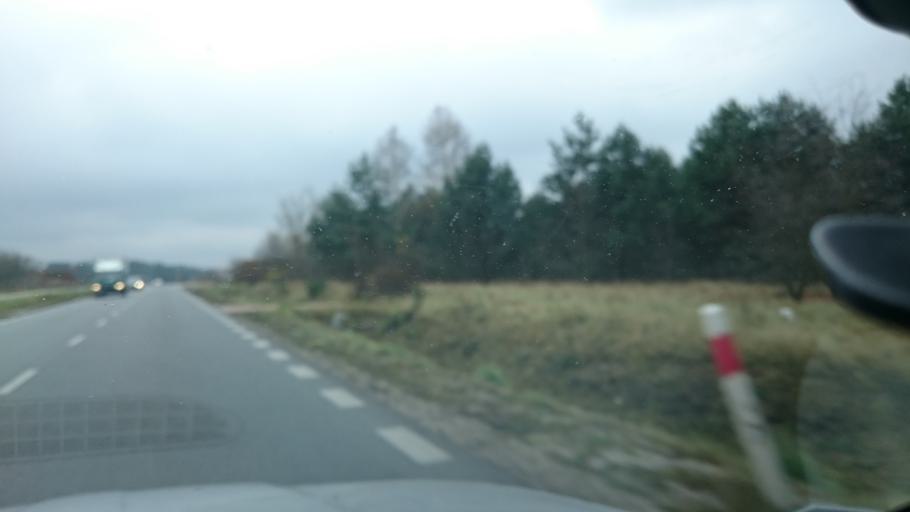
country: PL
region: Swietokrzyskie
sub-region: Powiat konecki
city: Konskie
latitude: 51.1330
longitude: 20.3617
